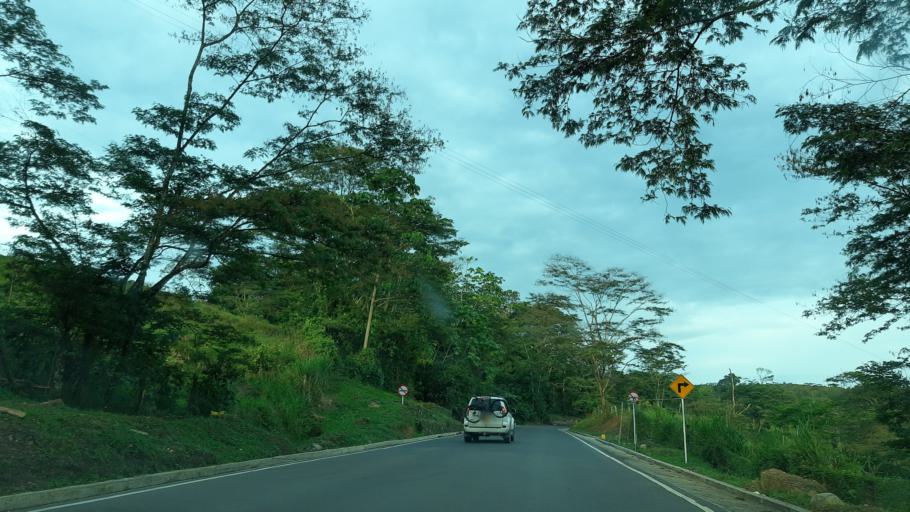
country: CO
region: Casanare
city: Sabanalarga
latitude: 4.8267
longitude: -73.0895
